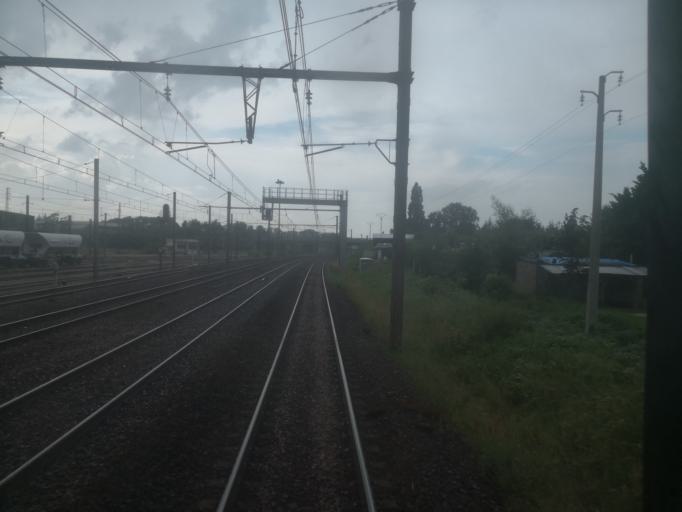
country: FR
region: Centre
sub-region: Departement du Loiret
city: Fleury-les-Aubrais
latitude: 47.9425
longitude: 1.8991
